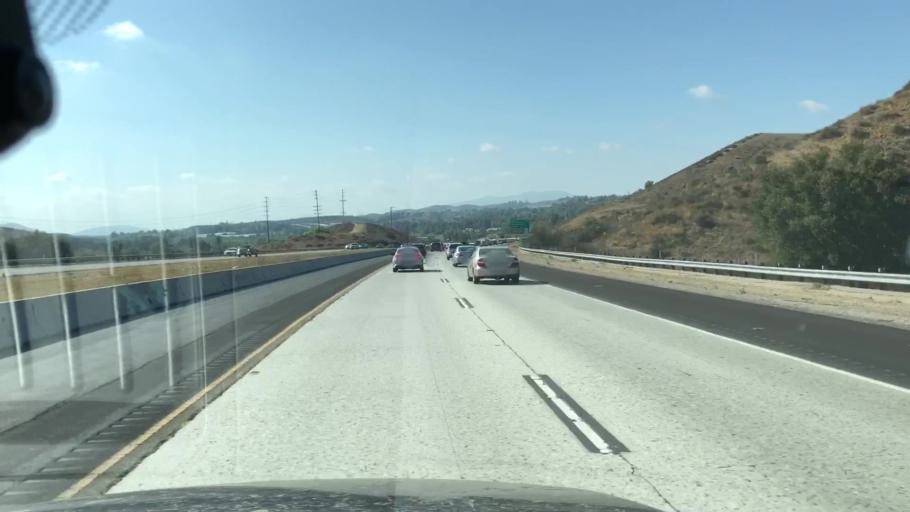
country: US
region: California
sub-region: Ventura County
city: Moorpark
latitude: 34.2924
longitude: -118.8306
